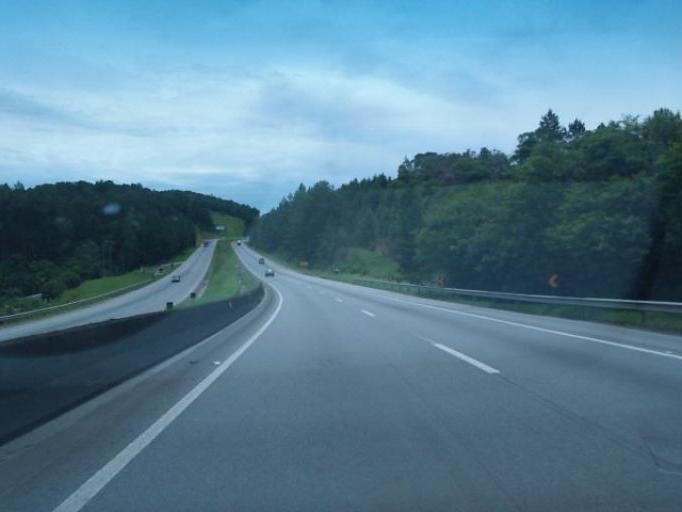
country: BR
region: Sao Paulo
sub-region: Juquitiba
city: Juquitiba
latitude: -23.9676
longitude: -47.1324
